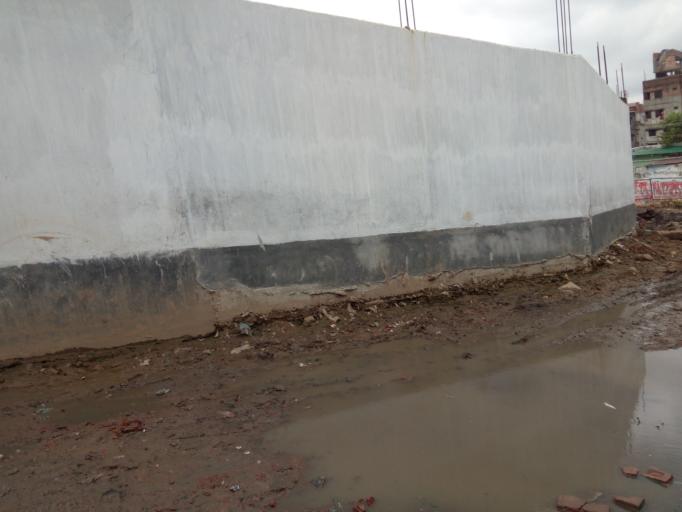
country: BD
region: Dhaka
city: Azimpur
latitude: 23.7264
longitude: 90.3711
